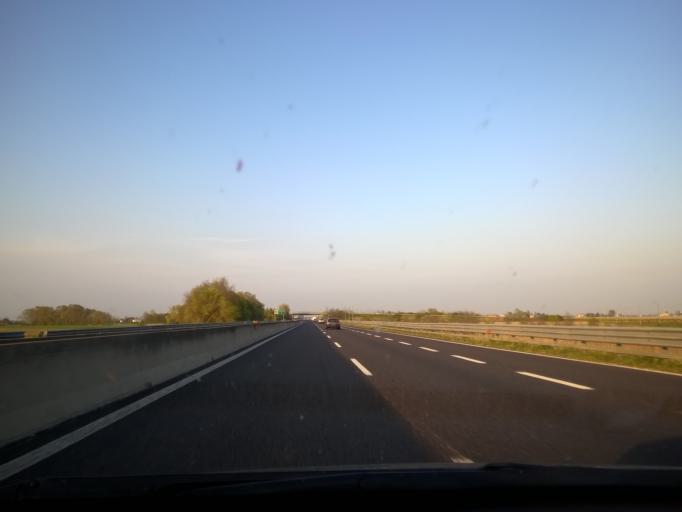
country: IT
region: Veneto
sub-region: Provincia di Rovigo
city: Fiesso Umbertiano
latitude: 44.9351
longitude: 11.6128
